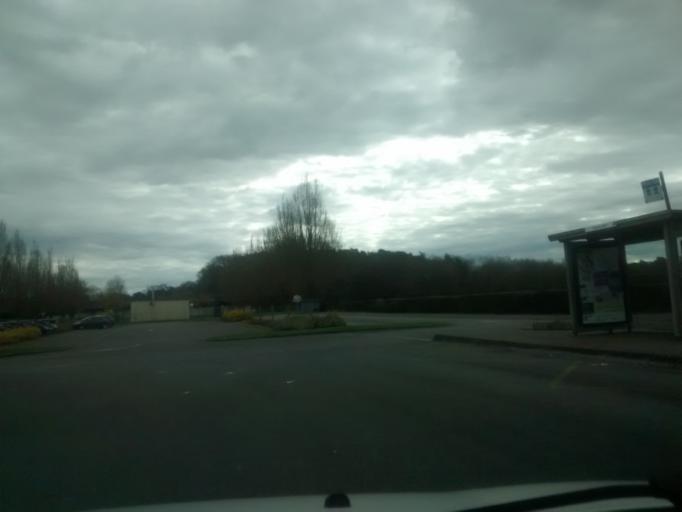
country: FR
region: Brittany
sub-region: Departement d'Ille-et-Vilaine
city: Fouillard
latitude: 48.1744
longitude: -1.6024
